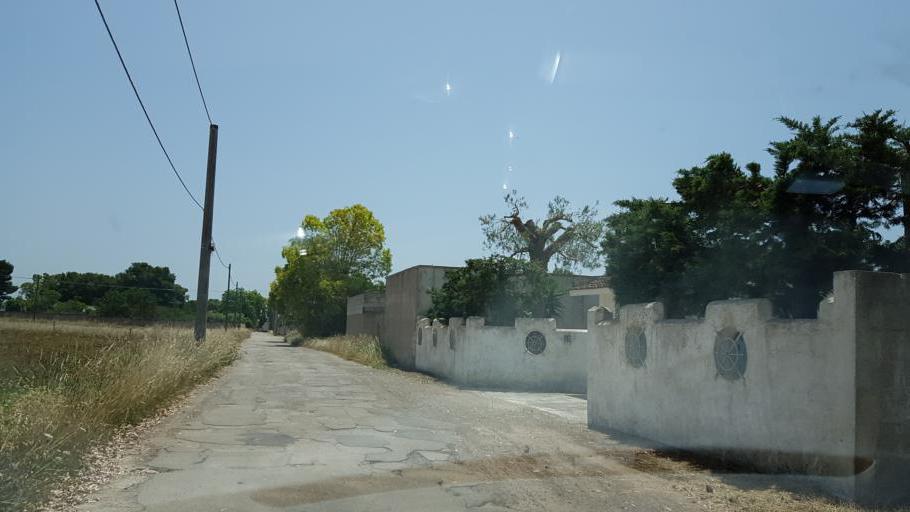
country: IT
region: Apulia
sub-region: Provincia di Lecce
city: Porto Cesareo
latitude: 40.2509
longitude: 17.9212
